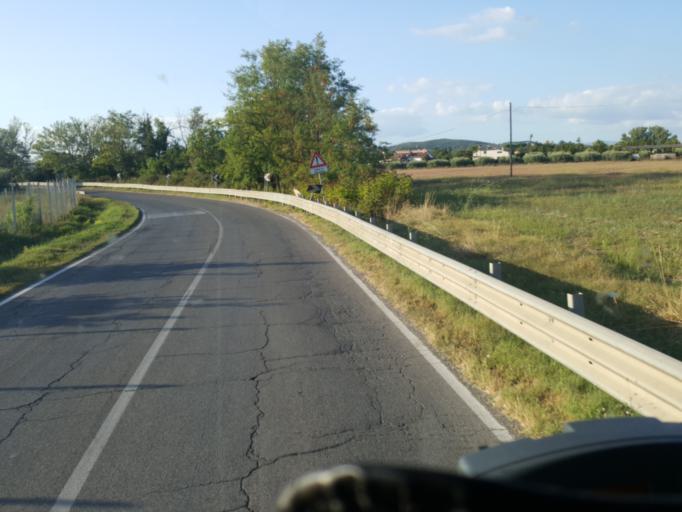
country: IT
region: Latium
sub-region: Citta metropolitana di Roma Capitale
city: Bivio di Capanelle
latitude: 42.1260
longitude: 12.5754
